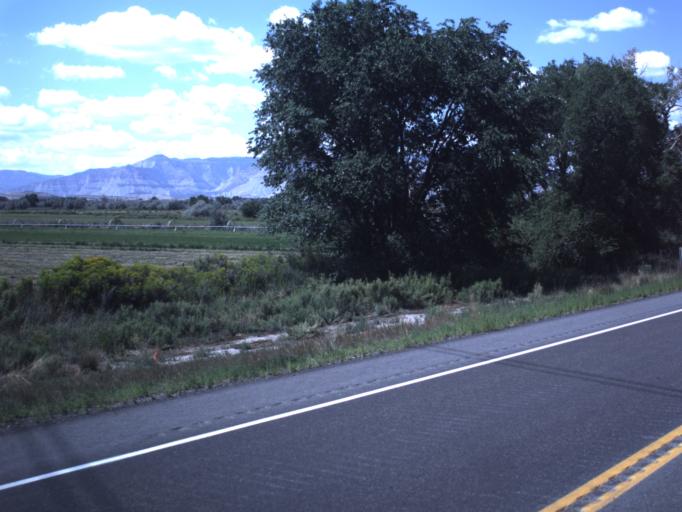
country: US
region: Utah
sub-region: Emery County
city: Huntington
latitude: 39.2993
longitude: -110.9645
